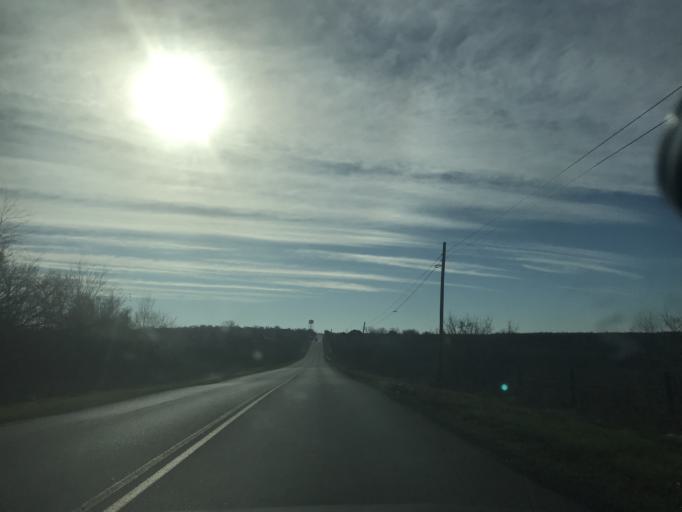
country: US
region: Texas
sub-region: Travis County
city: Manor
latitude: 30.3260
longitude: -97.5453
